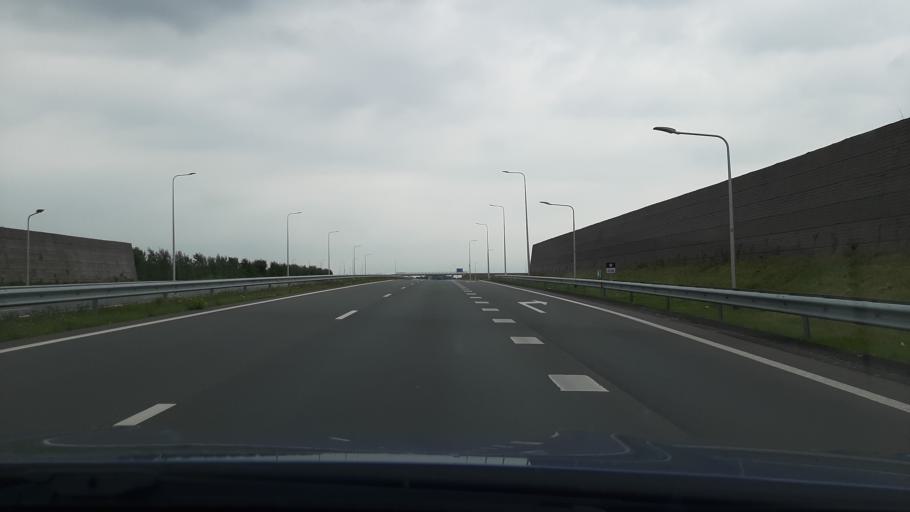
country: NL
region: North Holland
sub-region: Gemeente Medemblik
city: Medemblik
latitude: 52.6846
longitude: 5.1627
